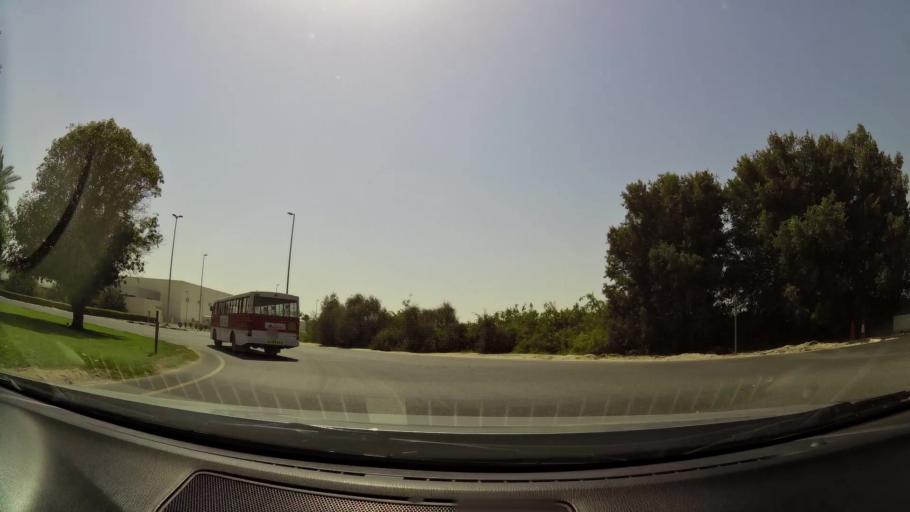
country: AE
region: Dubai
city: Dubai
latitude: 24.9732
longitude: 55.1641
